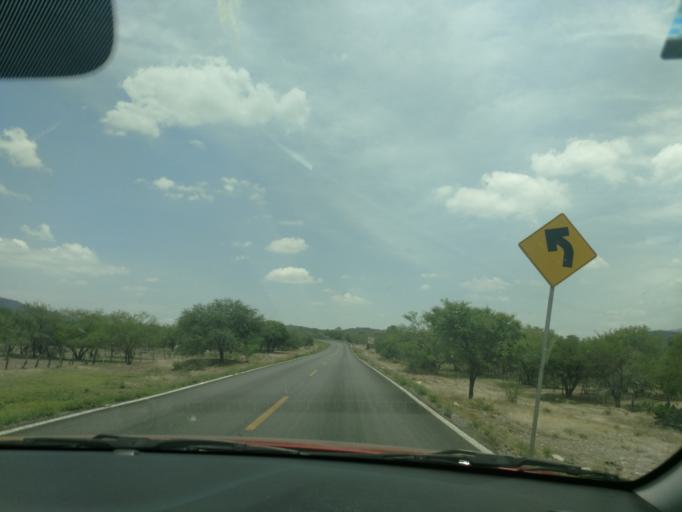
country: MX
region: San Luis Potosi
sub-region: Rioverde
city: Progreso
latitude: 22.0171
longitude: -100.3640
